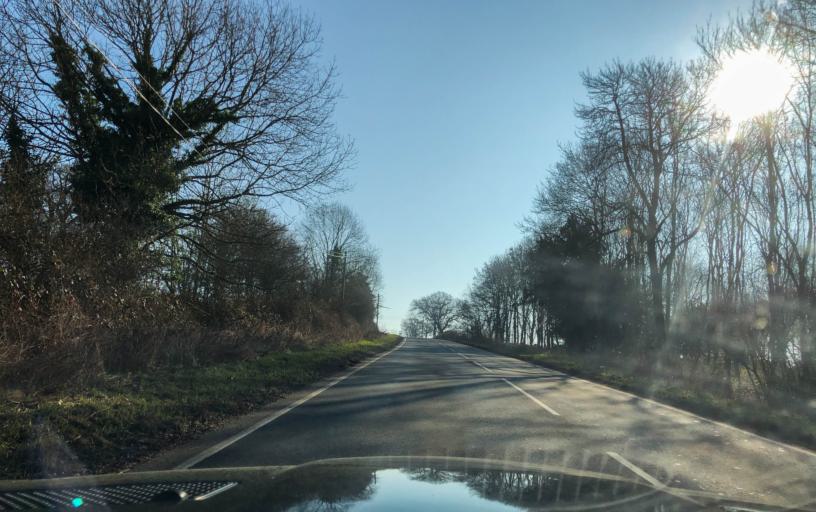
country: GB
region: England
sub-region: Warwickshire
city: Wellesbourne Mountford
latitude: 52.1784
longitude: -1.5686
